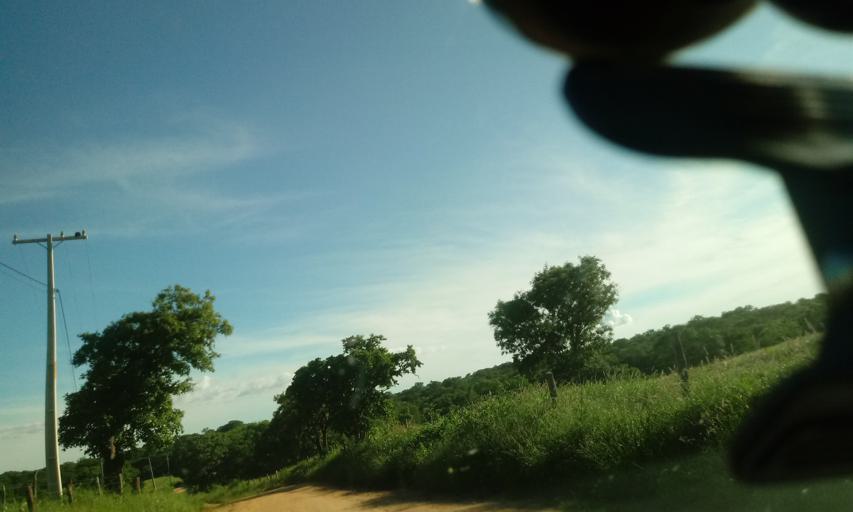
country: BR
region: Bahia
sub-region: Riacho De Santana
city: Riacho de Santana
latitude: -13.8309
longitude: -42.7680
